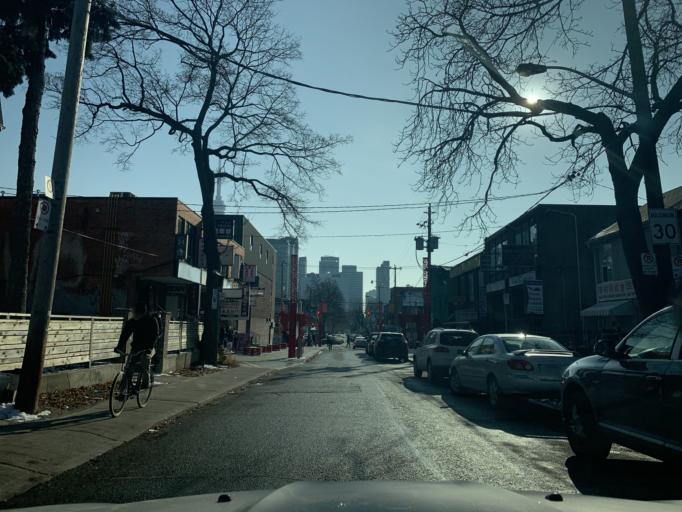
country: CA
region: Ontario
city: Toronto
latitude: 43.6541
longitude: -79.3964
